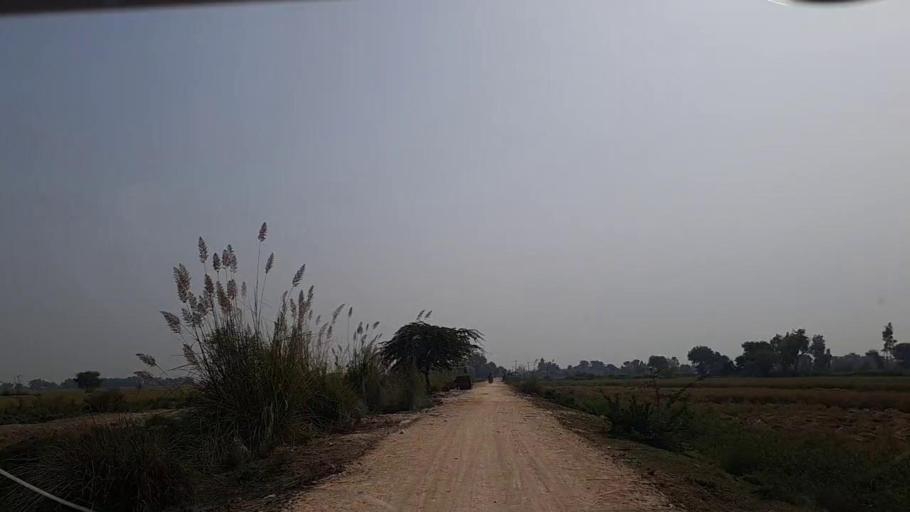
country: PK
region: Sindh
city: Garhi Yasin
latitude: 27.9252
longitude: 68.5664
